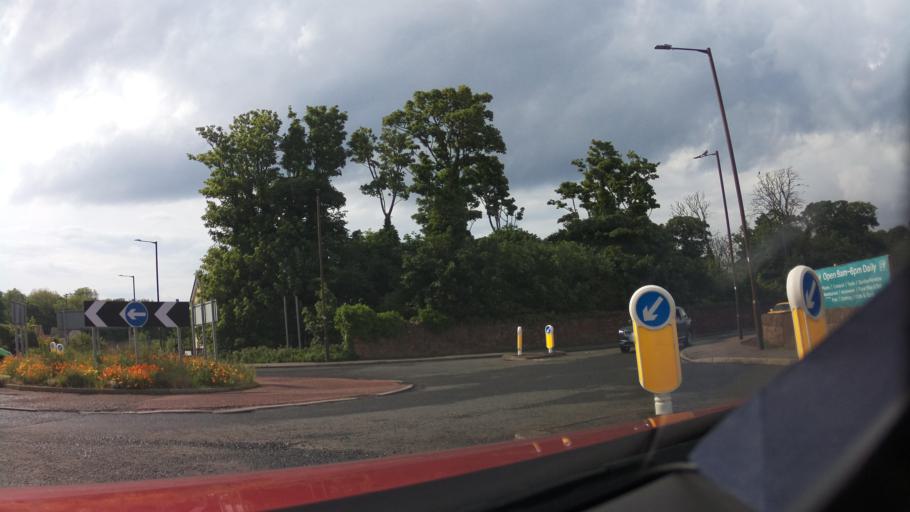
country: GB
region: Scotland
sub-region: East Lothian
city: Dunbar
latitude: 55.9906
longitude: -2.5110
